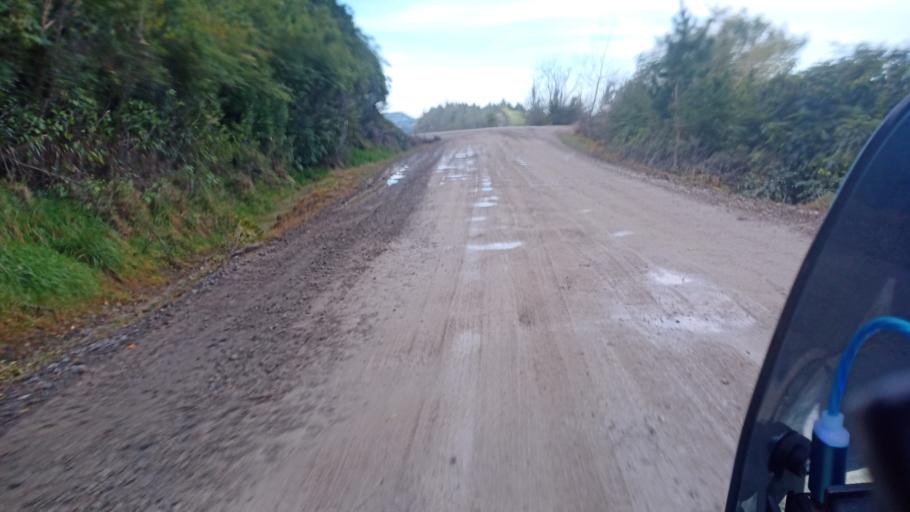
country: NZ
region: Gisborne
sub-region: Gisborne District
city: Gisborne
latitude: -38.1419
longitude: 178.1929
